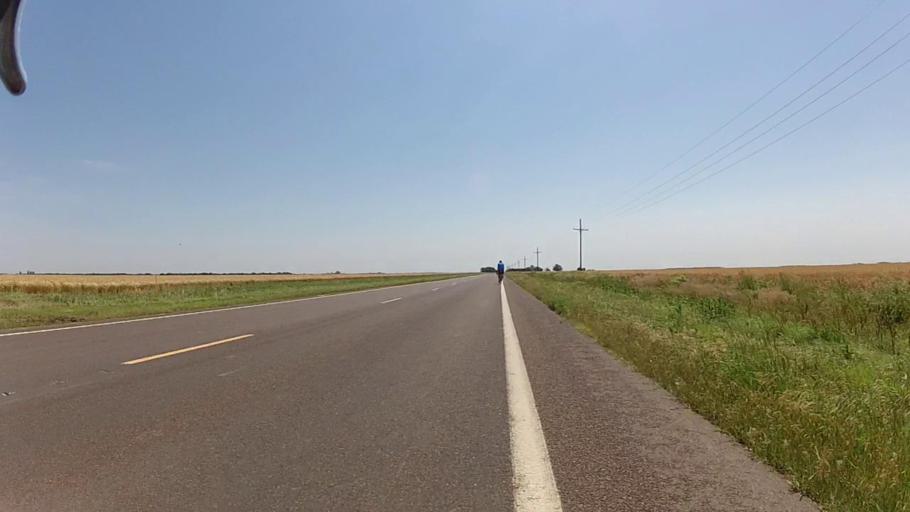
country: US
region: Kansas
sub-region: Sumner County
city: Caldwell
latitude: 37.0329
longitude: -97.5555
